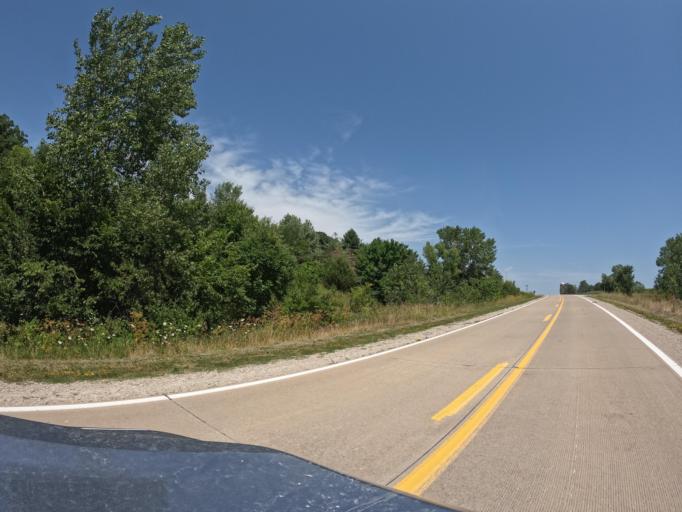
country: US
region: Iowa
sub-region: Henry County
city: Mount Pleasant
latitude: 40.9878
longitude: -91.6518
